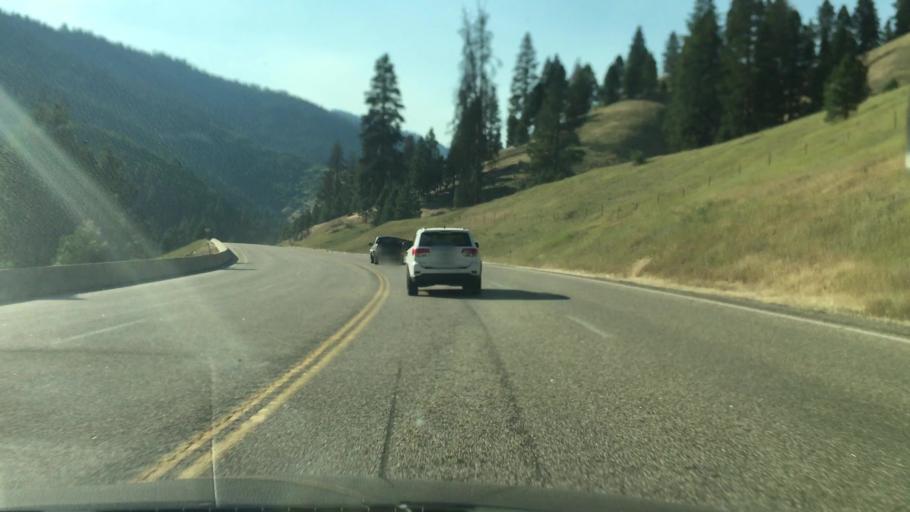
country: US
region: Idaho
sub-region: Boise County
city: Idaho City
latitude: 44.1104
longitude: -116.0996
